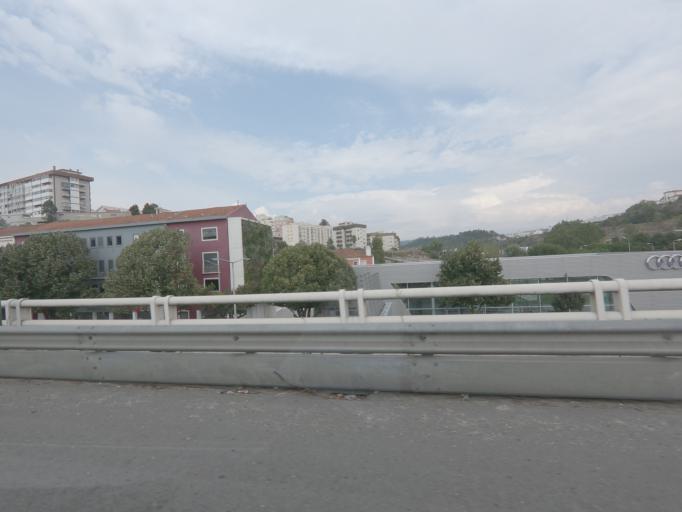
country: PT
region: Coimbra
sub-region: Coimbra
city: Coimbra
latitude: 40.2202
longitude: -8.4392
